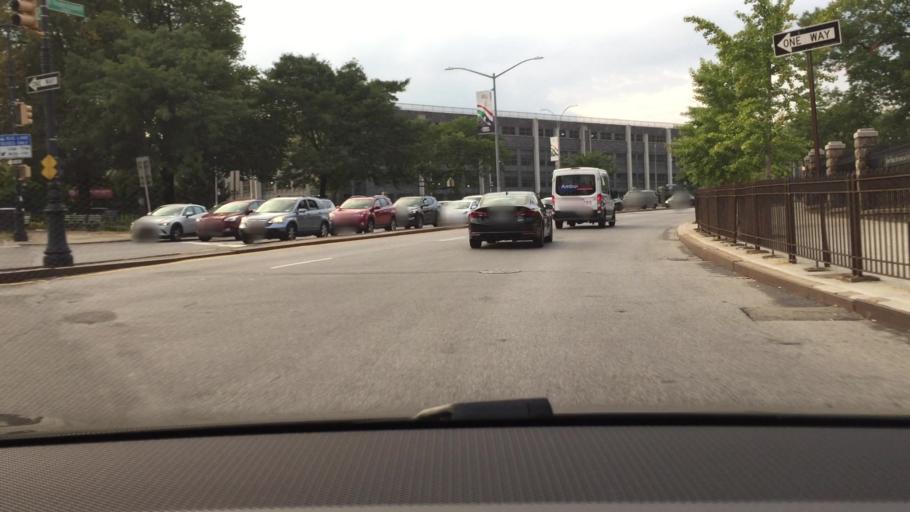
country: US
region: New York
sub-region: Bronx
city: The Bronx
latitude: 40.8576
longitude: -73.8807
